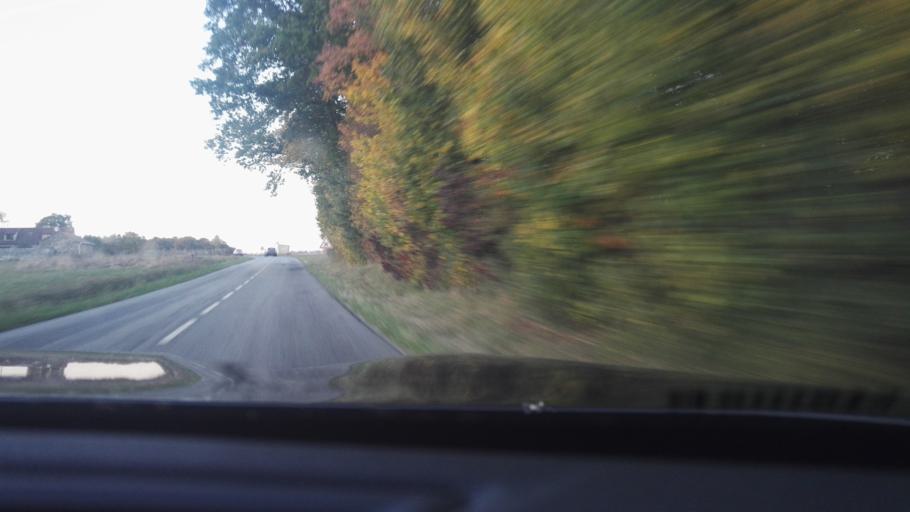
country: FR
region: Ile-de-France
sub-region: Departement des Yvelines
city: Longnes
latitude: 48.8993
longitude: 1.5838
